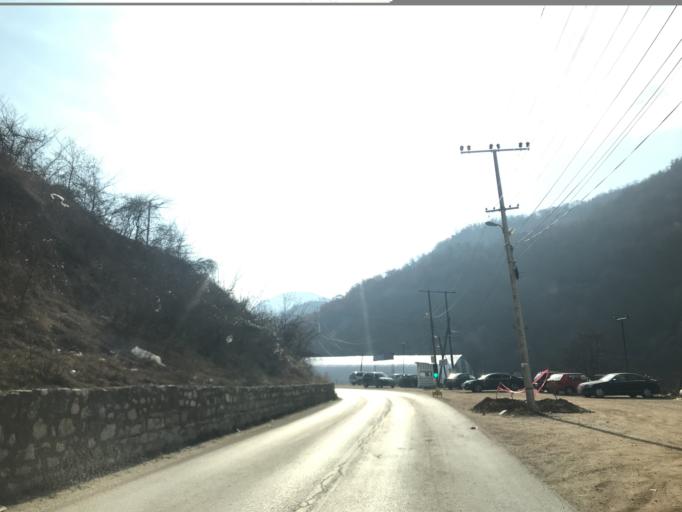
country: XK
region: Prizren
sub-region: Prizren
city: Prizren
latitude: 42.2105
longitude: 20.7480
